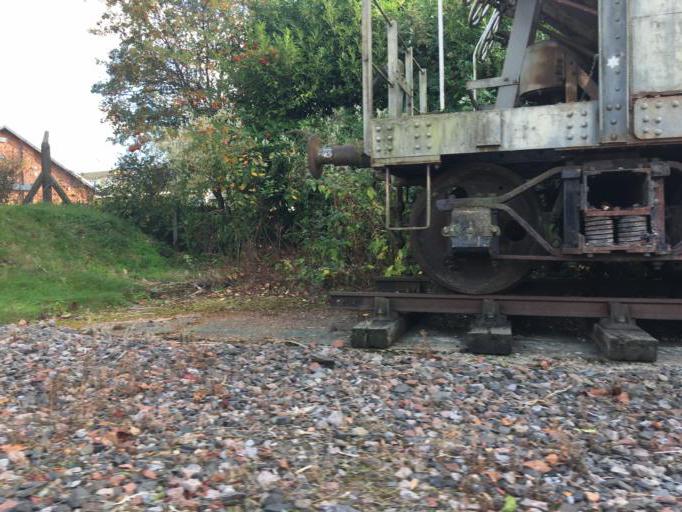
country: GB
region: England
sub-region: City of York
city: York
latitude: 53.9598
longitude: -1.0986
